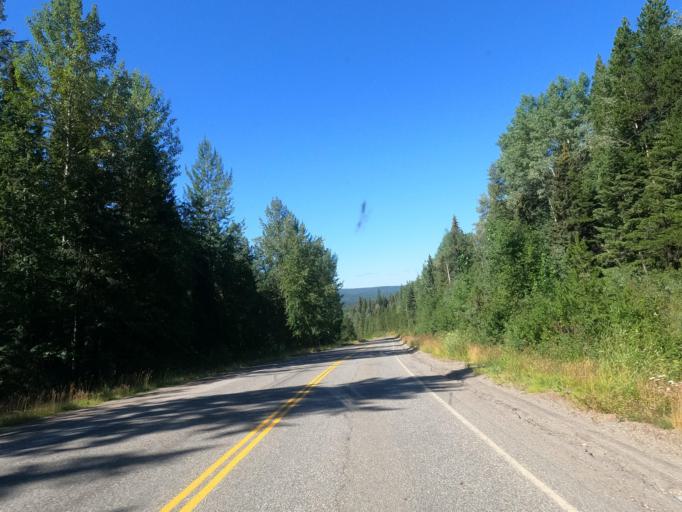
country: CA
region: British Columbia
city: Quesnel
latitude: 53.0225
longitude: -122.0609
